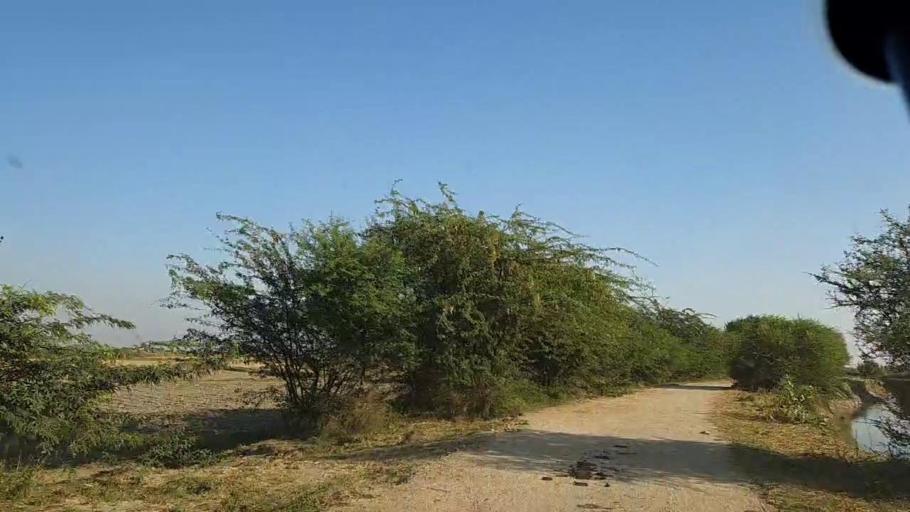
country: PK
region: Sindh
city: Chuhar Jamali
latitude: 24.5627
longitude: 68.0684
